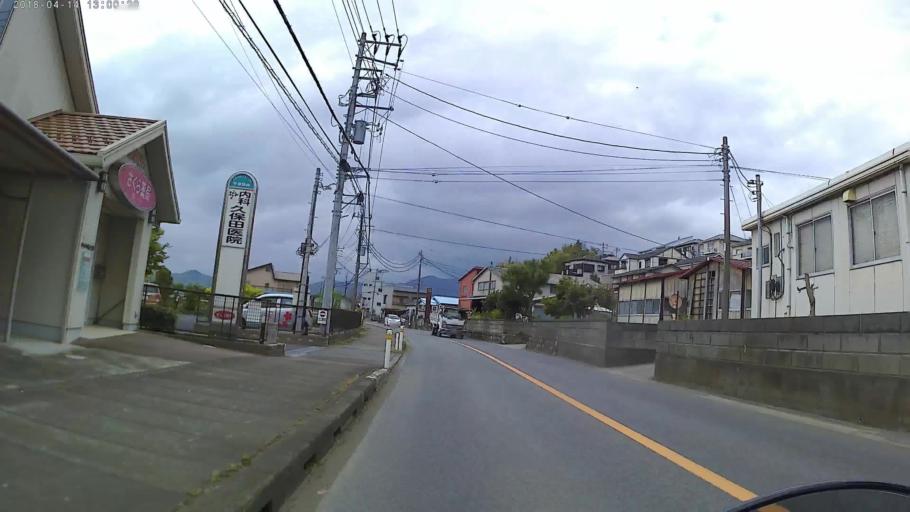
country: JP
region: Kanagawa
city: Isehara
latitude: 35.3720
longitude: 139.3061
